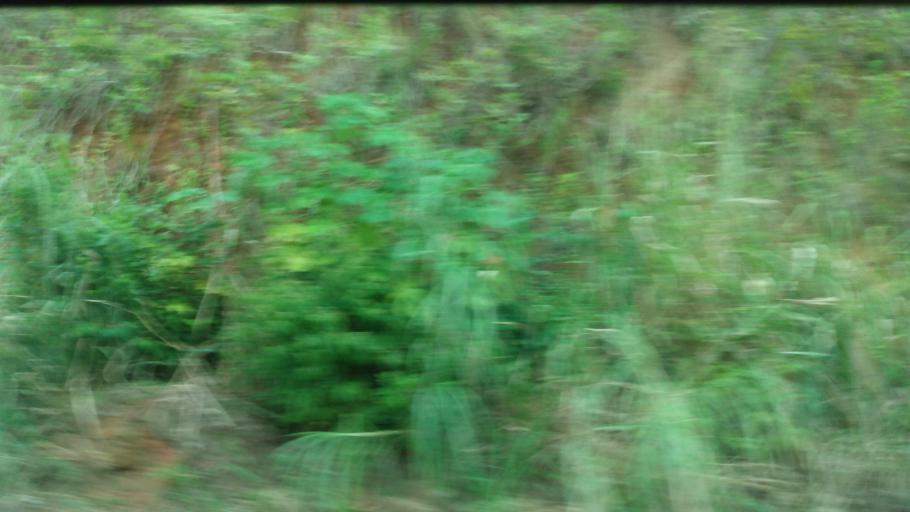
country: BR
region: Pernambuco
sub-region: Maraial
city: Maraial
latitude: -8.7243
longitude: -35.7895
